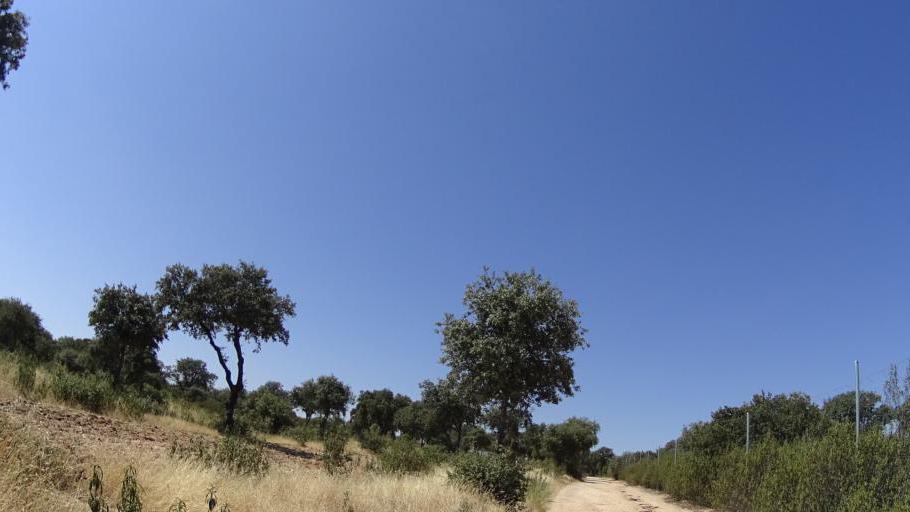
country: ES
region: Madrid
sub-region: Provincia de Madrid
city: Majadahonda
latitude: 40.4408
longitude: -3.8659
